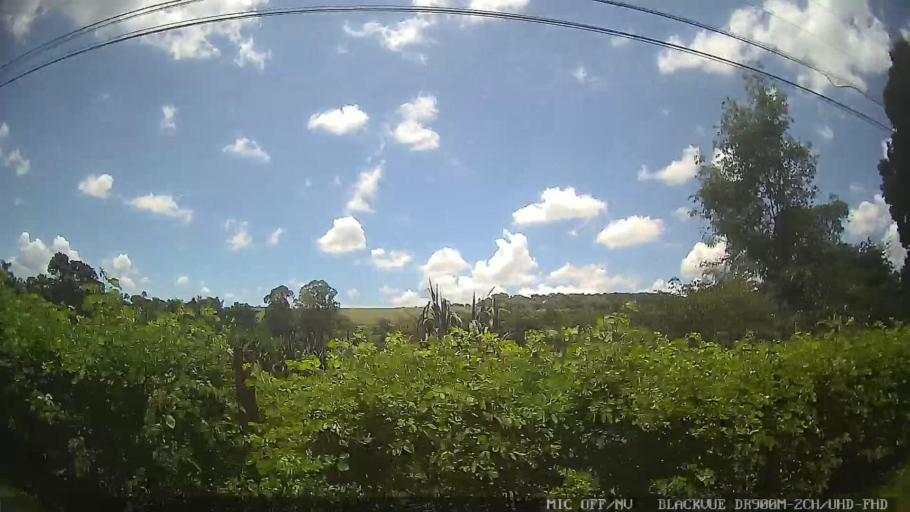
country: BR
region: Sao Paulo
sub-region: Atibaia
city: Atibaia
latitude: -23.0492
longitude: -46.5038
